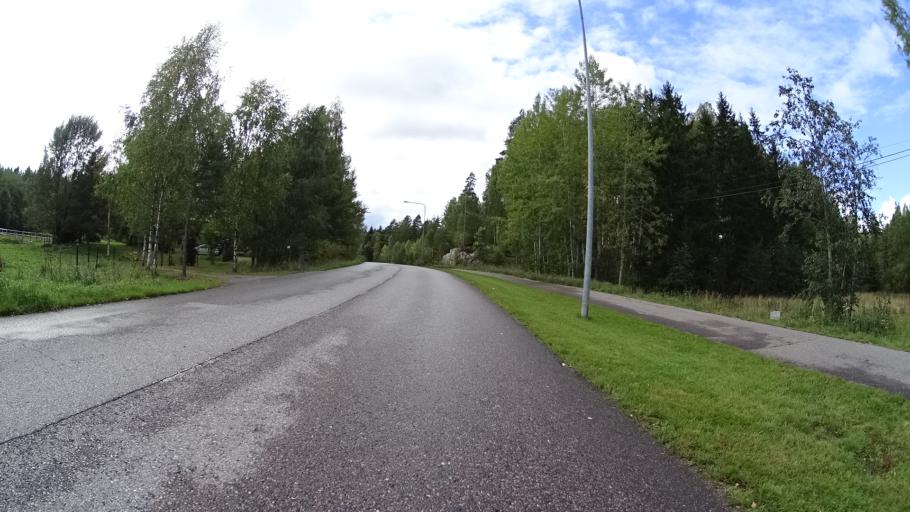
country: FI
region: Uusimaa
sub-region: Helsinki
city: Espoo
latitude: 60.2429
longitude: 24.6469
